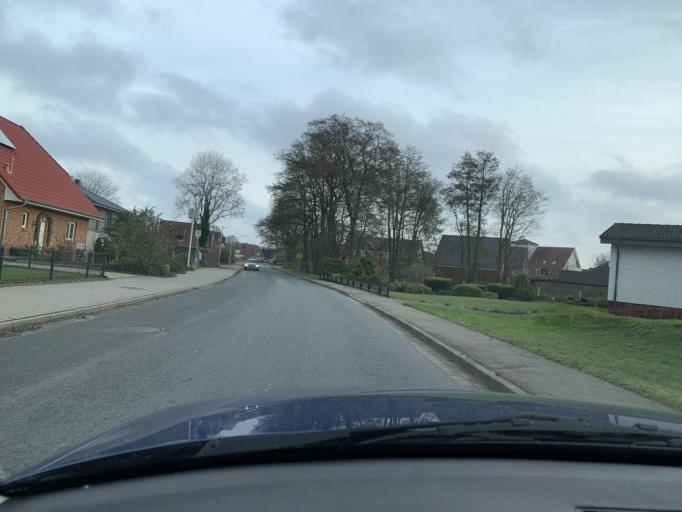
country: DE
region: Schleswig-Holstein
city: Wesseln
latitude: 54.2046
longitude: 9.0831
